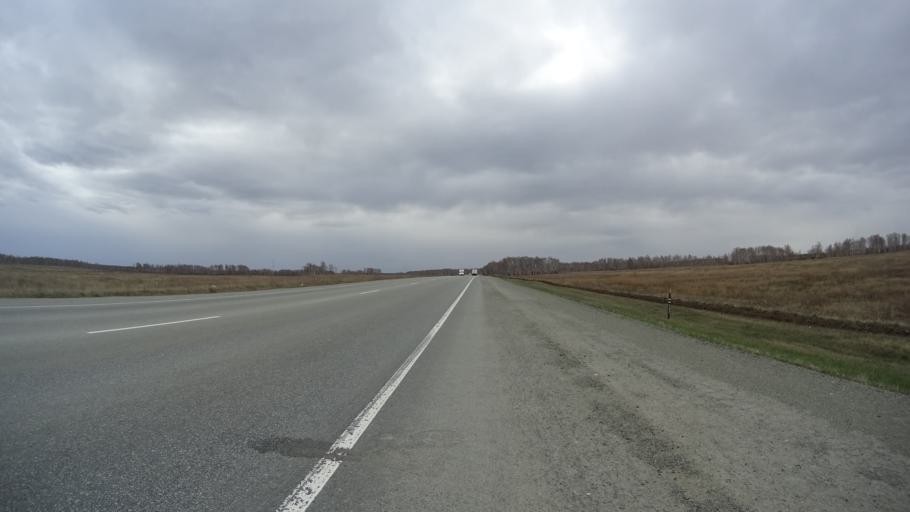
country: RU
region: Chelyabinsk
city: Yemanzhelinsk
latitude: 54.7029
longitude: 61.2543
